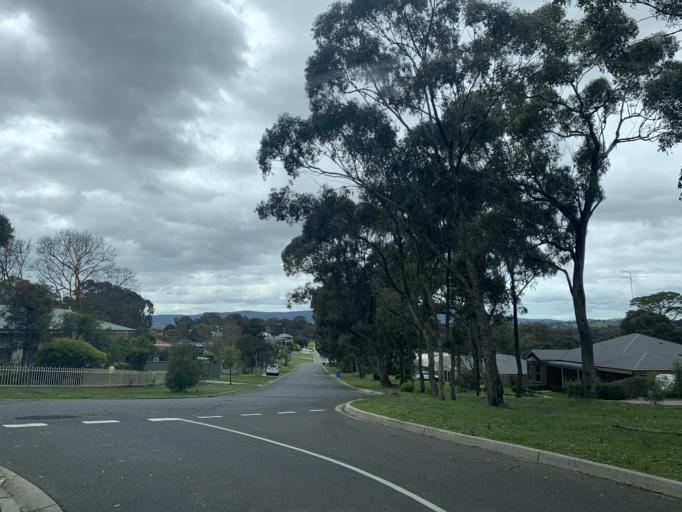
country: AU
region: Victoria
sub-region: Whittlesea
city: Whittlesea
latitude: -37.2119
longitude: 145.0445
